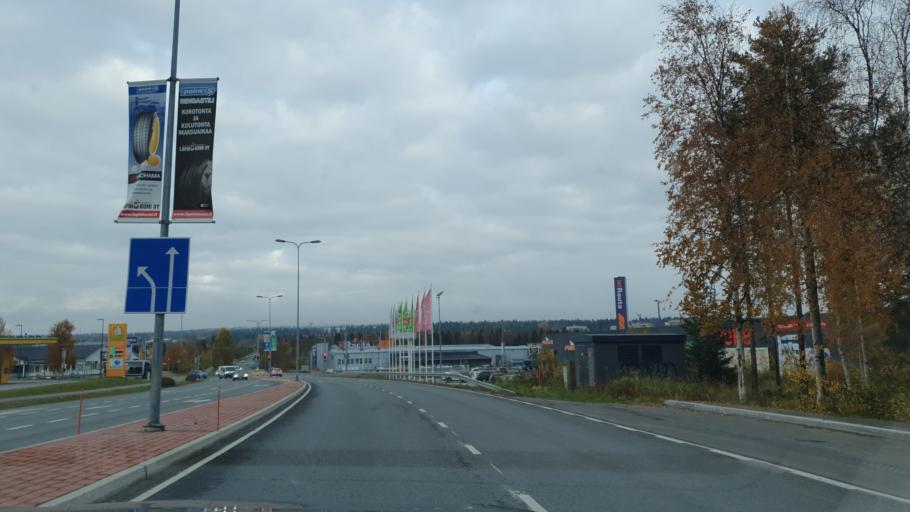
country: FI
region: Lapland
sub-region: Rovaniemi
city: Rovaniemi
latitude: 66.4920
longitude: 25.6924
